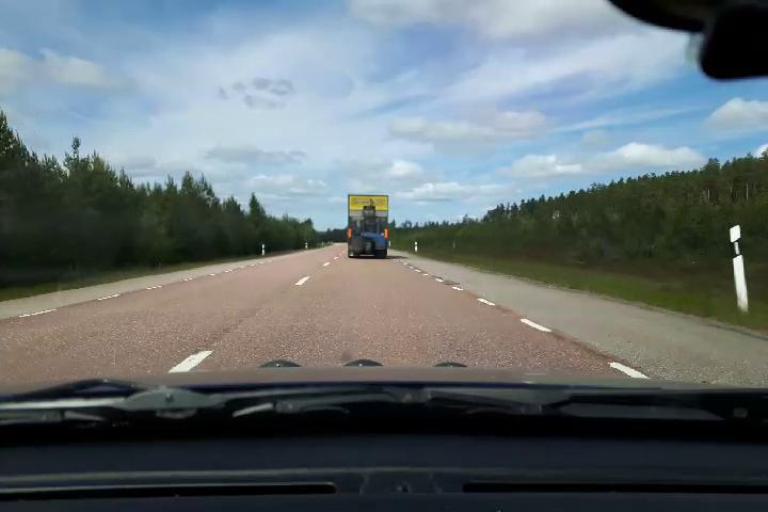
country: SE
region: Uppsala
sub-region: Osthammars Kommun
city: Bjorklinge
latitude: 60.1685
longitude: 17.4901
